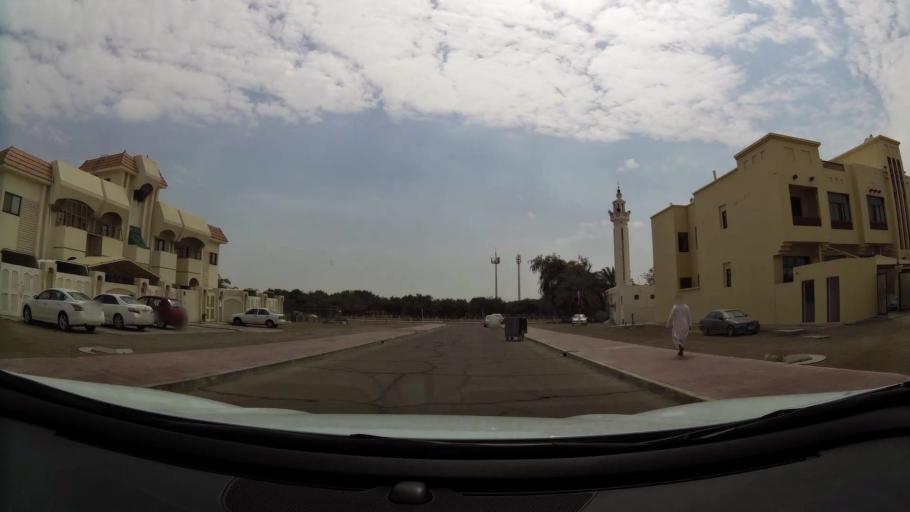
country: AE
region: Abu Dhabi
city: Al Ain
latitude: 24.2118
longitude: 55.7900
